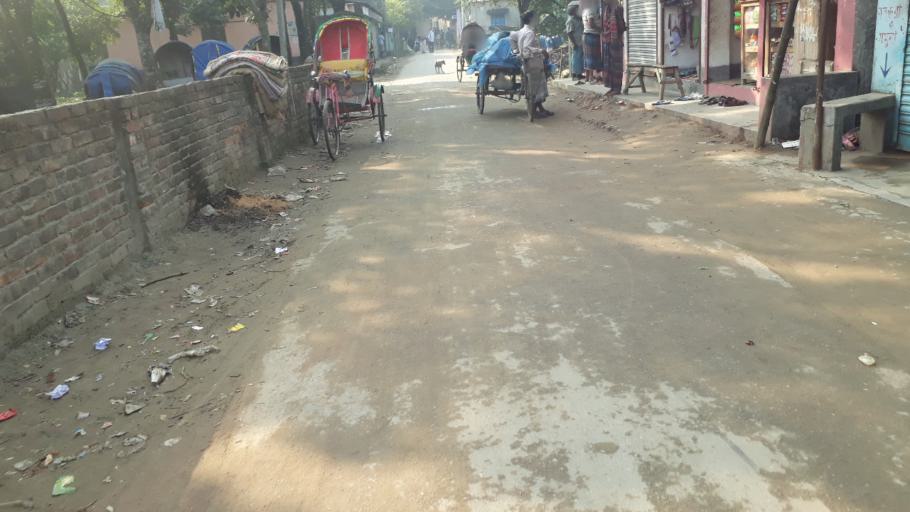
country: BD
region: Dhaka
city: Tungi
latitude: 23.8854
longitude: 90.2618
